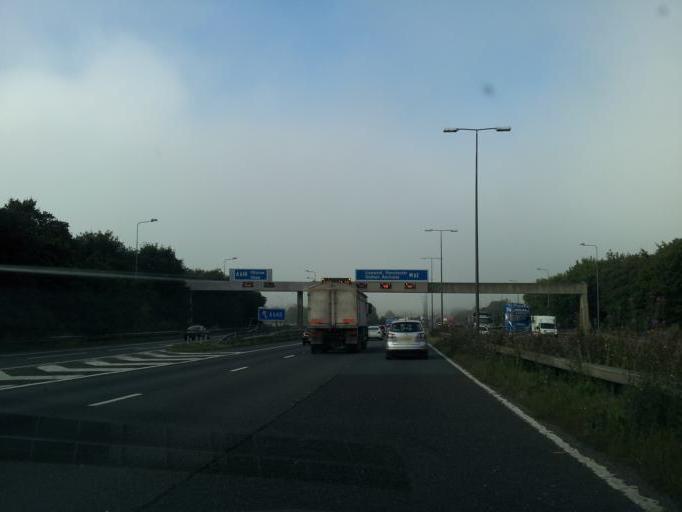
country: GB
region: England
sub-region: Borough of Rochdale
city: Milnrow
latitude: 53.6044
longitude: -2.1040
